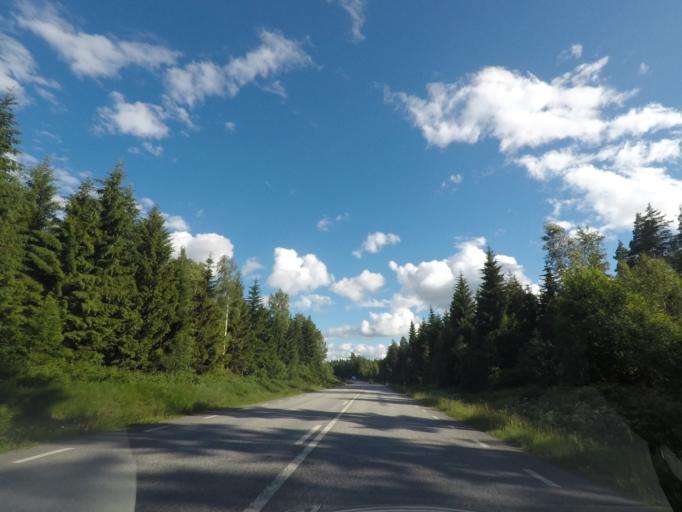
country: SE
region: OErebro
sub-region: Lindesbergs Kommun
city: Frovi
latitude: 59.4848
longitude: 15.3775
